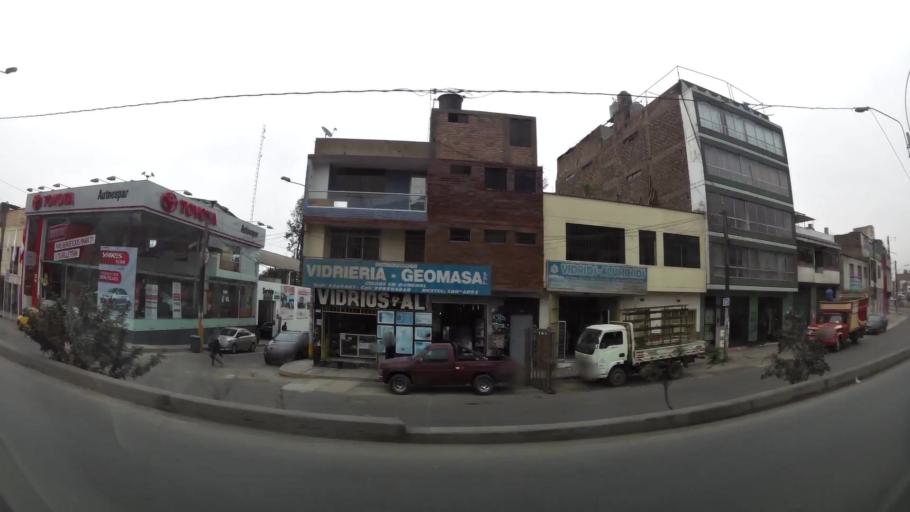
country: PE
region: Lima
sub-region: Lima
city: Independencia
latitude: -11.9500
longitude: -77.0494
